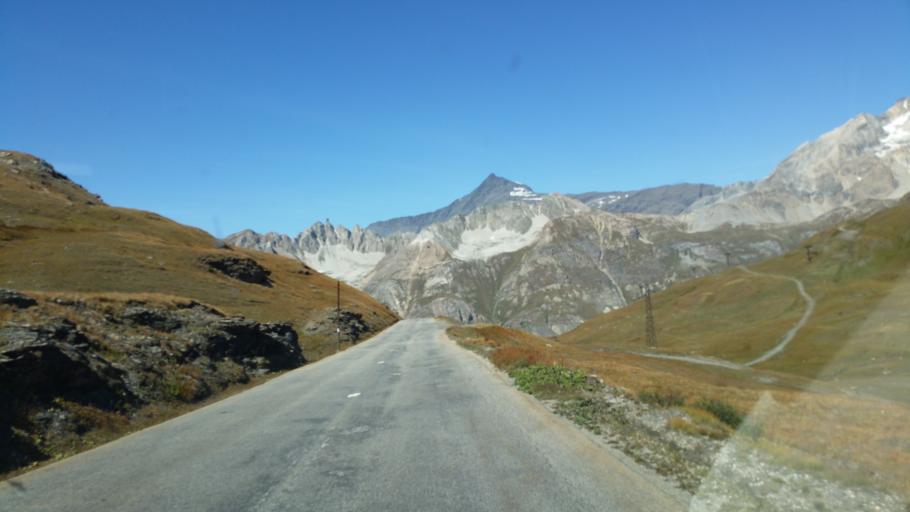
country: FR
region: Rhone-Alpes
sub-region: Departement de la Savoie
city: Val-d'Isere
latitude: 45.4266
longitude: 7.0222
